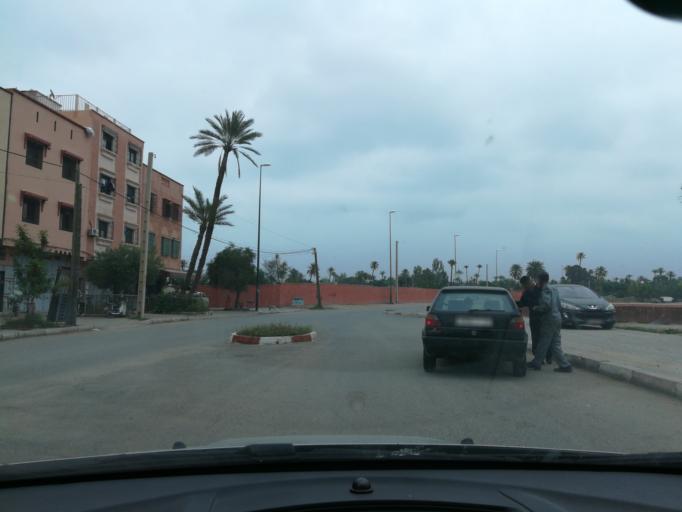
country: MA
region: Marrakech-Tensift-Al Haouz
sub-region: Marrakech
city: Marrakesh
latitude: 31.6628
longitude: -7.9843
